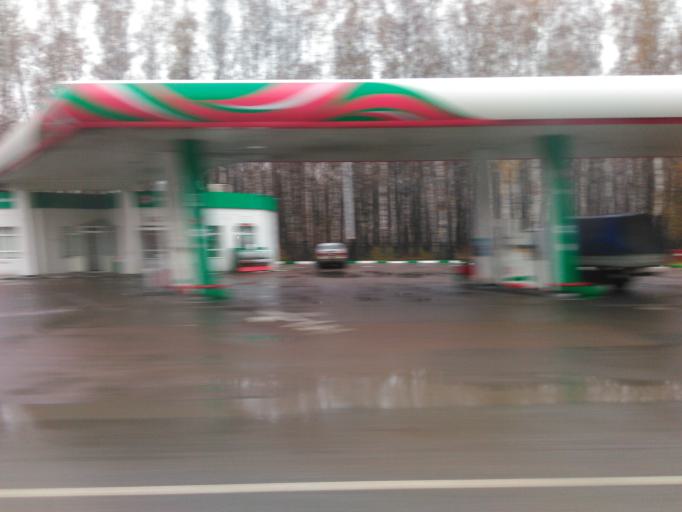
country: RU
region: Tatarstan
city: Osinovo
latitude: 55.8380
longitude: 48.8507
